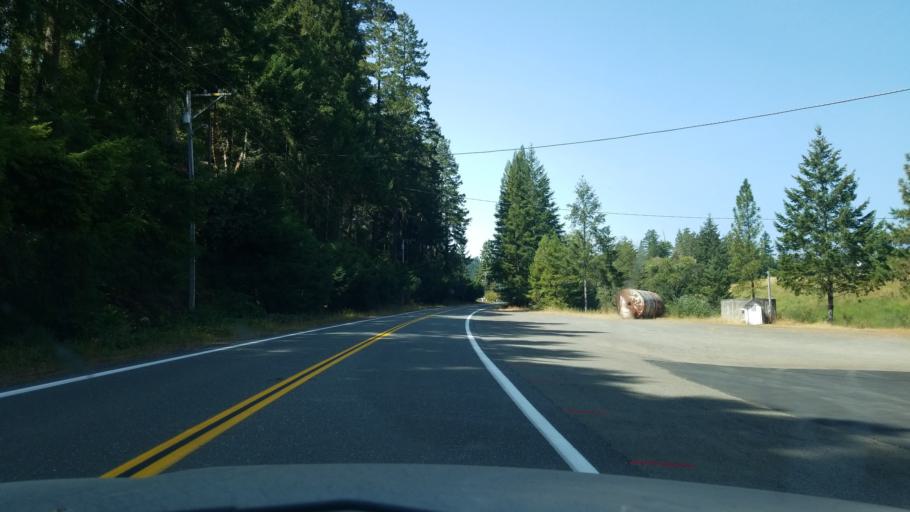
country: US
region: California
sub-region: Mendocino County
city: Laytonville
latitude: 39.8496
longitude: -123.7139
